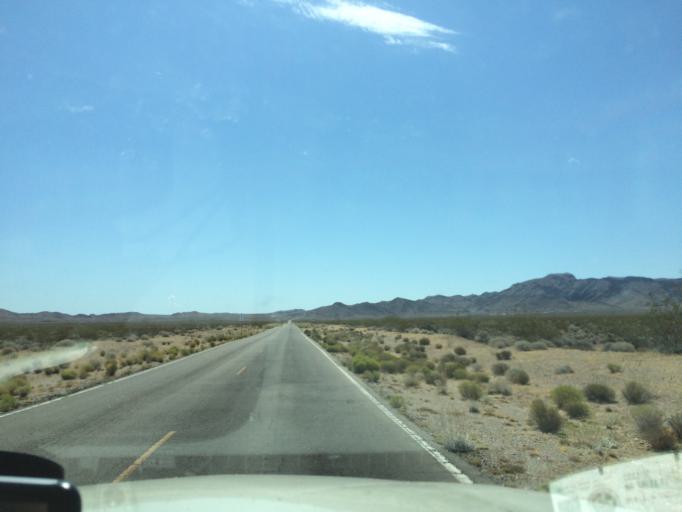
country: US
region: Nevada
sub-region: Clark County
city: Moapa Town
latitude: 36.4542
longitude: -114.7090
